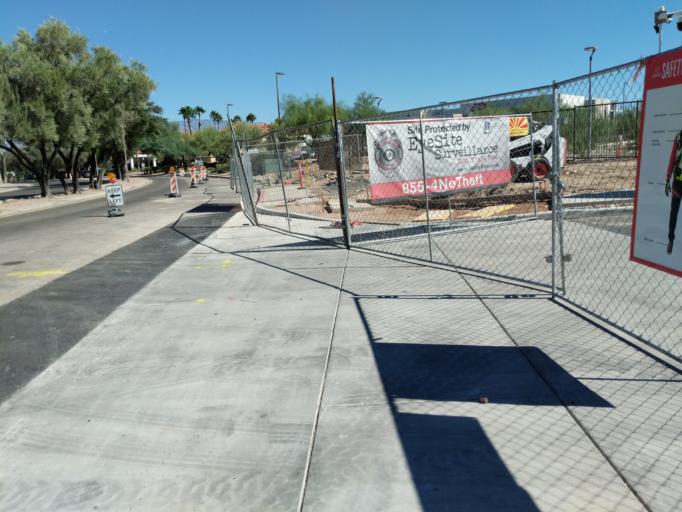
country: US
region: Arizona
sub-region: Pima County
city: Tucson
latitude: 32.2185
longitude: -110.8801
